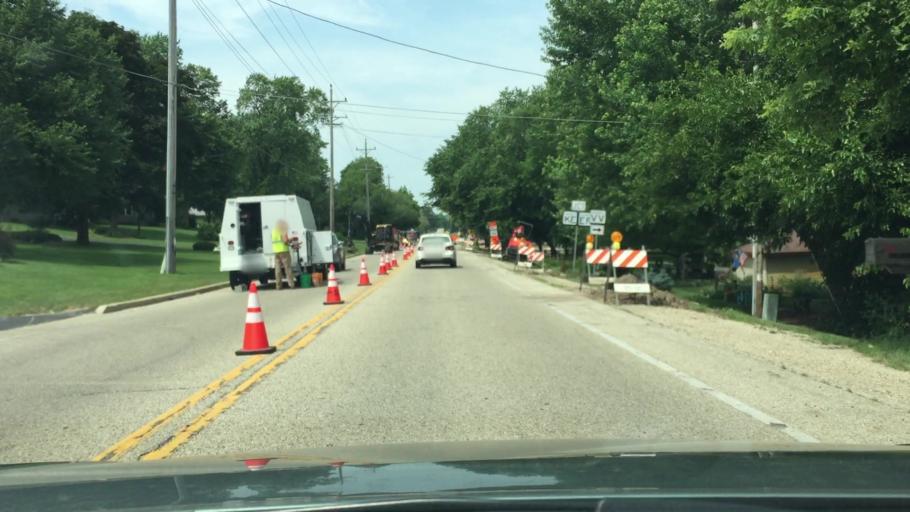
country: US
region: Wisconsin
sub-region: Waukesha County
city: Merton
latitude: 43.1413
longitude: -88.3043
